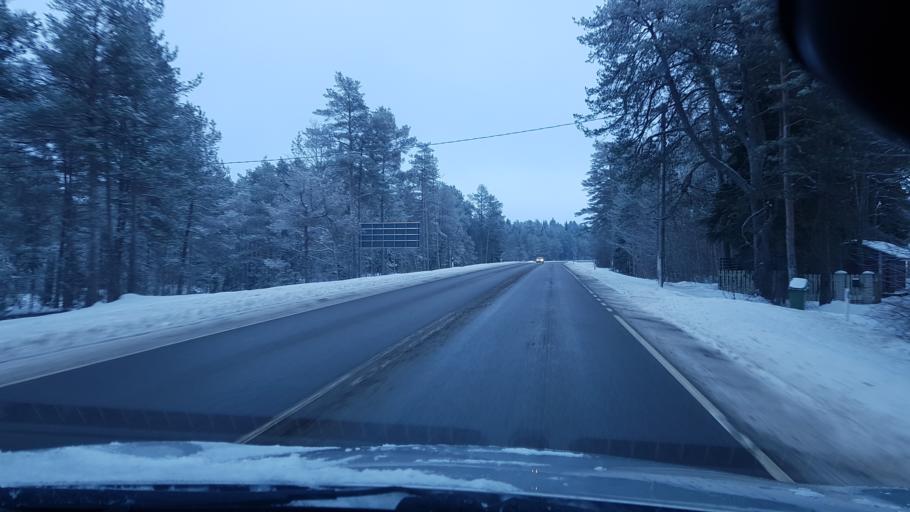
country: EE
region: Harju
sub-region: Keila linn
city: Keila
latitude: 59.3352
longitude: 24.2837
